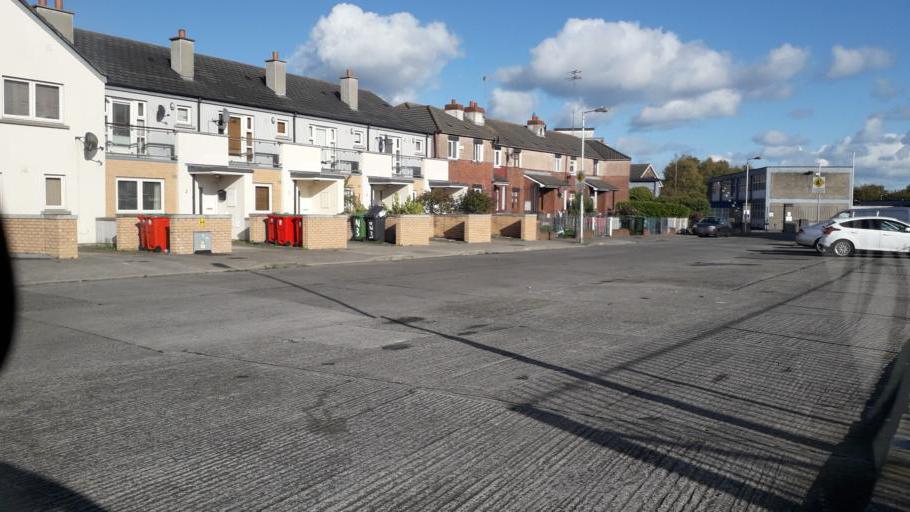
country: IE
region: Leinster
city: Raheny
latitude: 53.3891
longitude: -6.1820
